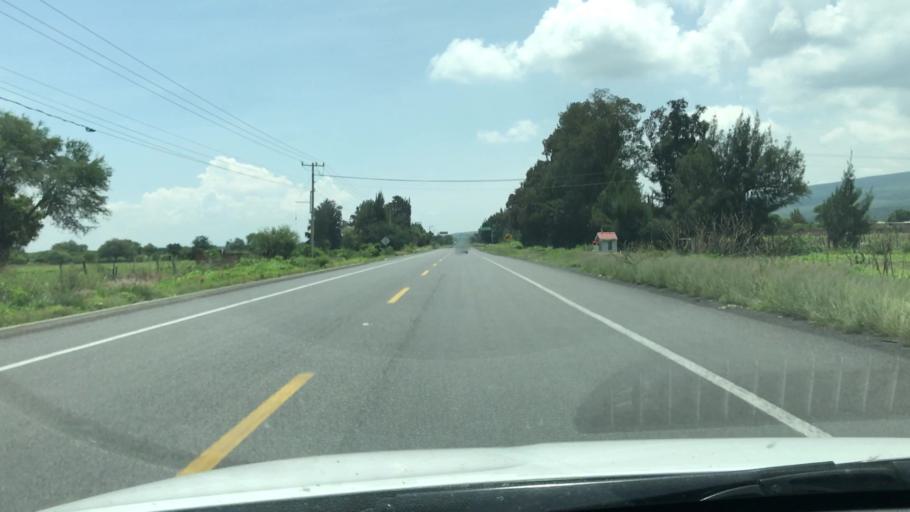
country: MX
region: Michoacan
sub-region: Yurecuaro
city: Yurecuaro
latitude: 20.3398
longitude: -102.1780
